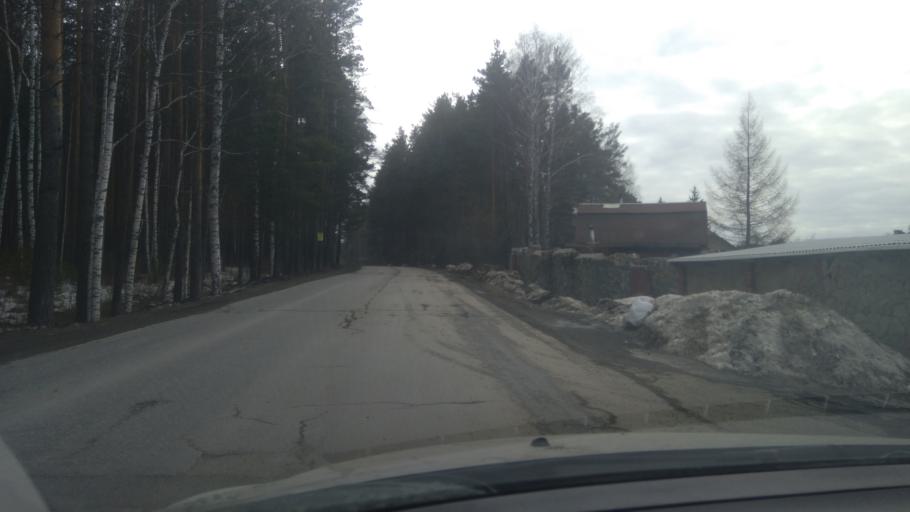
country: RU
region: Sverdlovsk
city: Severka
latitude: 56.8405
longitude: 60.3853
